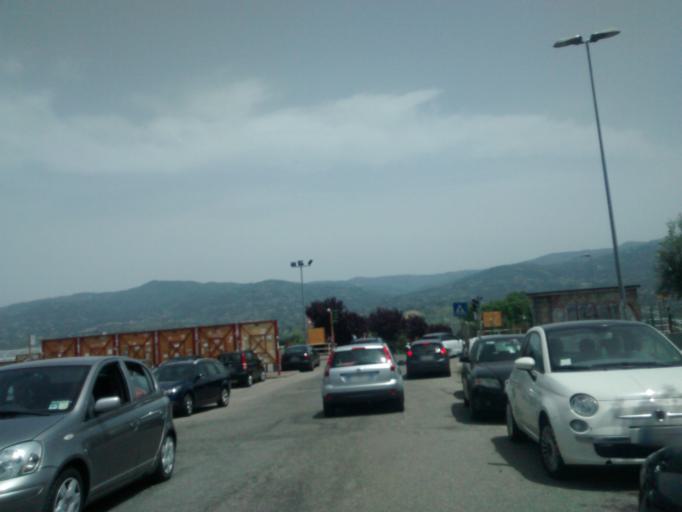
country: IT
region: Calabria
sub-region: Provincia di Cosenza
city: Arcavacata
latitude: 39.3644
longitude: 16.2253
